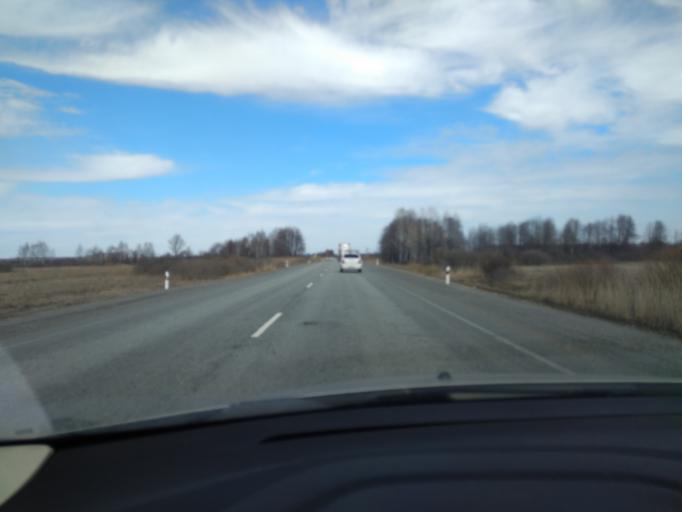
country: RU
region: Sverdlovsk
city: Pyshma
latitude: 57.0222
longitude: 63.3962
